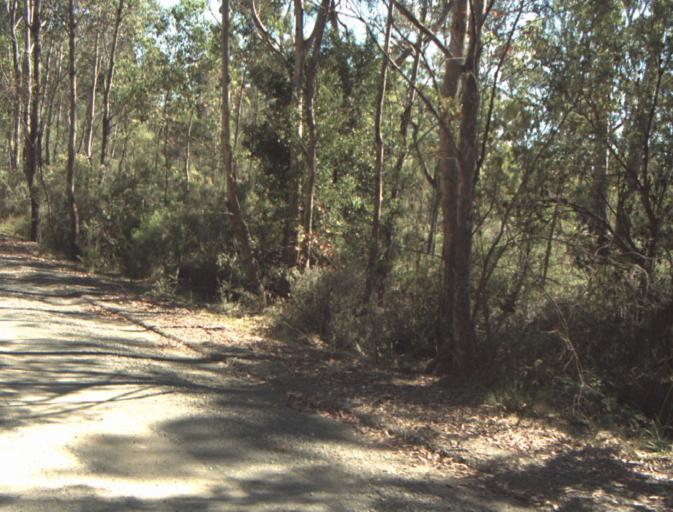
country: AU
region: Tasmania
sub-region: Launceston
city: Mayfield
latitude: -41.3405
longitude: 147.2101
